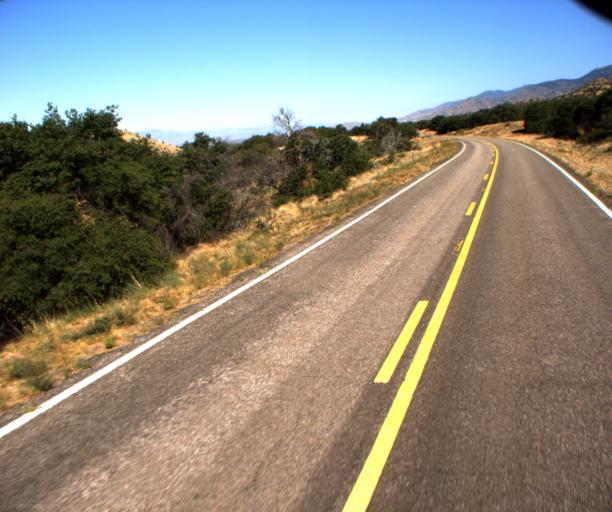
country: US
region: Arizona
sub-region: Graham County
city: Swift Trail Junction
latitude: 32.5953
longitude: -109.8586
